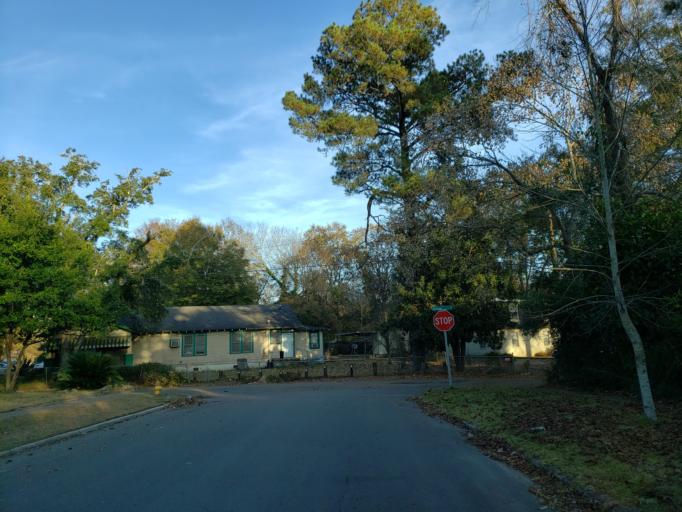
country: US
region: Mississippi
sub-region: Forrest County
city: Hattiesburg
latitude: 31.3302
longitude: -89.2975
